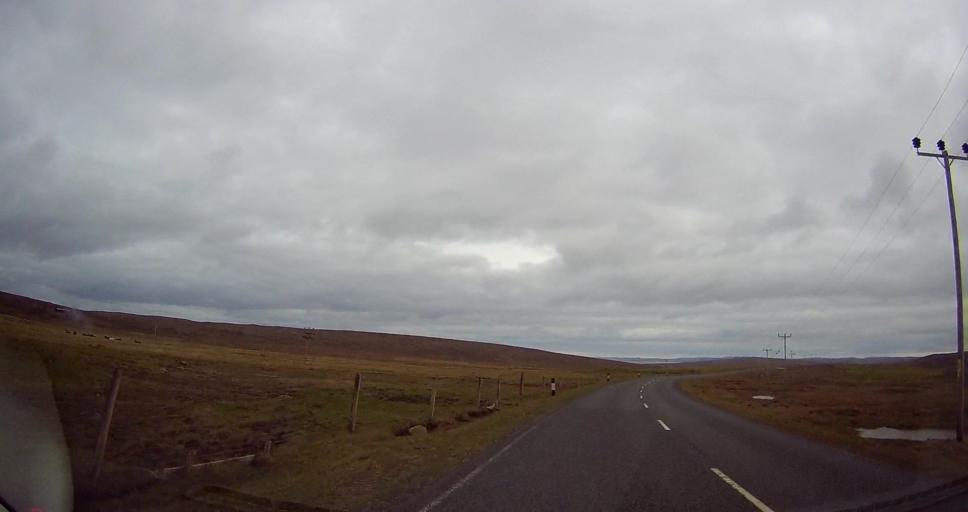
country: GB
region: Scotland
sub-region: Shetland Islands
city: Shetland
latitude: 60.7325
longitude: -0.8952
